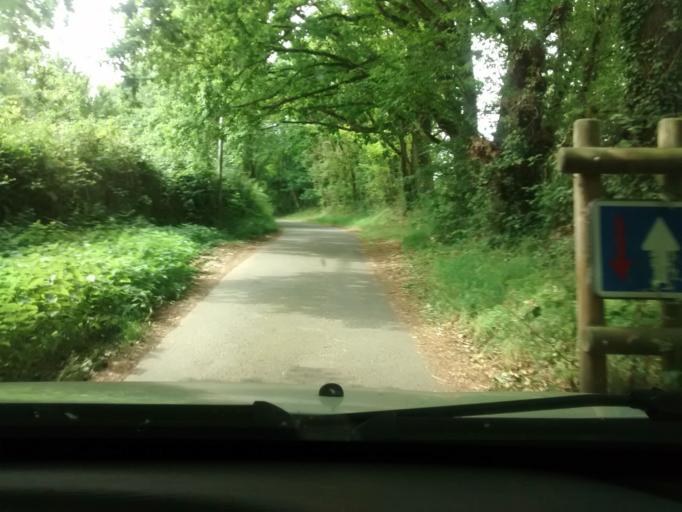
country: FR
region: Brittany
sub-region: Departement d'Ille-et-Vilaine
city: Saint-Jacques-de-la-Lande
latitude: 48.0880
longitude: -1.7292
